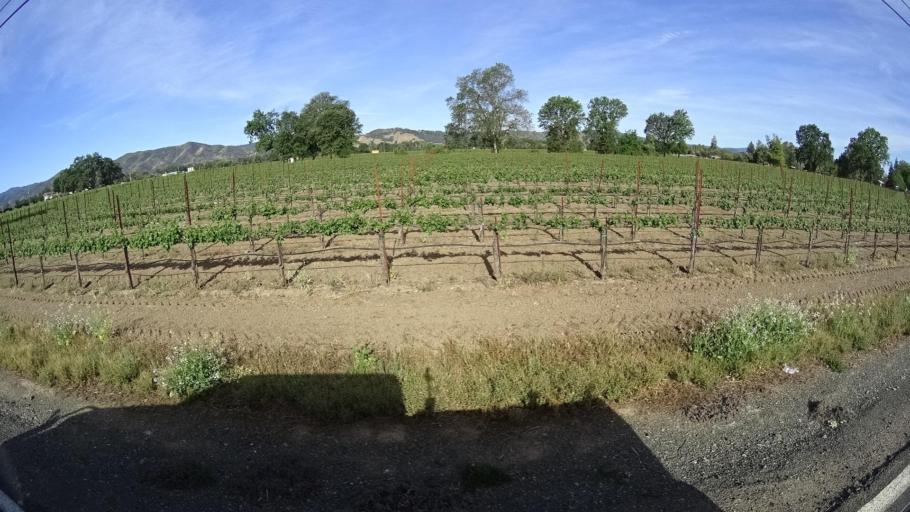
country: US
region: California
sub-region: Lake County
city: Lakeport
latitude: 39.0051
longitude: -122.8849
